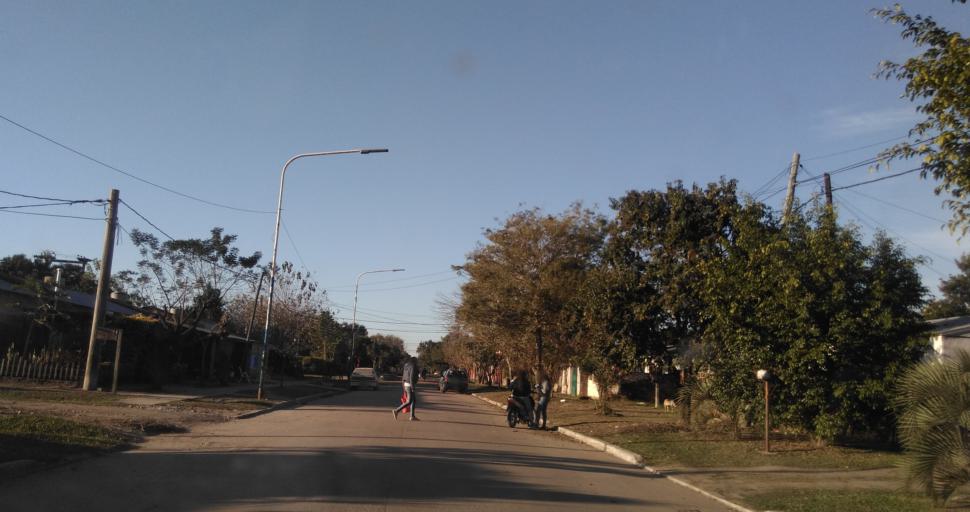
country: AR
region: Chaco
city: Colonia Benitez
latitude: -27.3341
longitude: -58.9427
